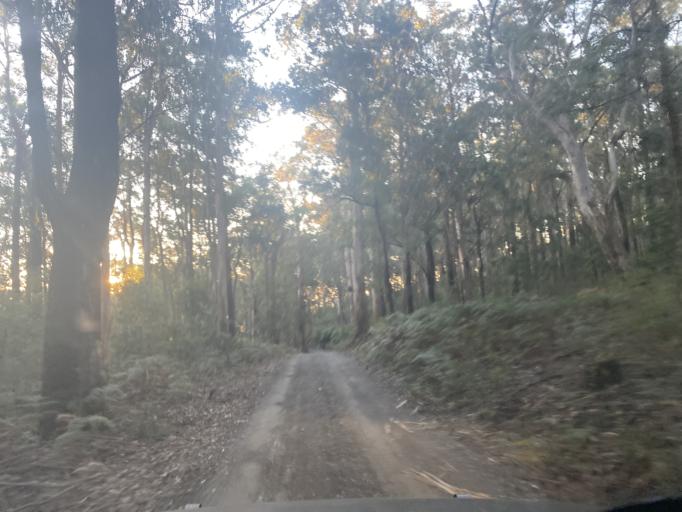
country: AU
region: Victoria
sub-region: Yarra Ranges
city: Healesville
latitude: -37.4341
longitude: 145.5316
